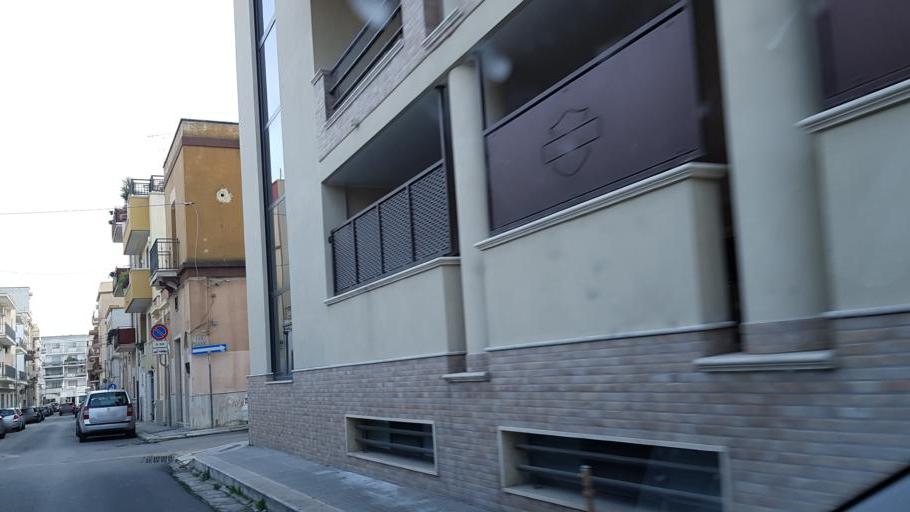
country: IT
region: Apulia
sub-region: Provincia di Brindisi
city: Brindisi
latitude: 40.6348
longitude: 17.9314
